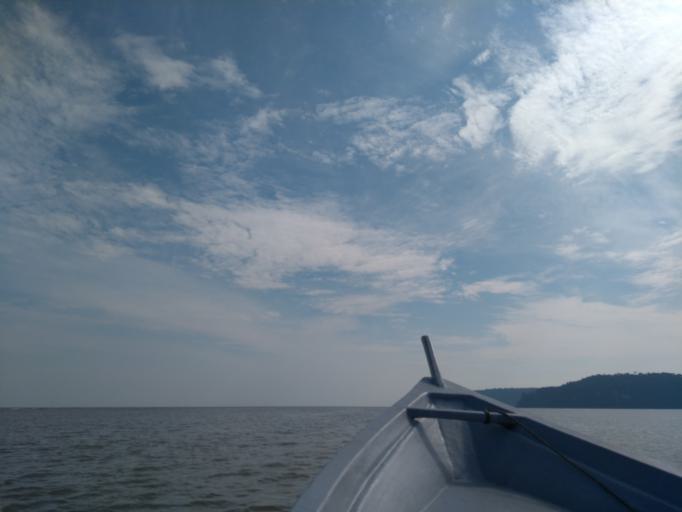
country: MY
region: Sarawak
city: Kuching
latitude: 1.7025
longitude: 110.4297
